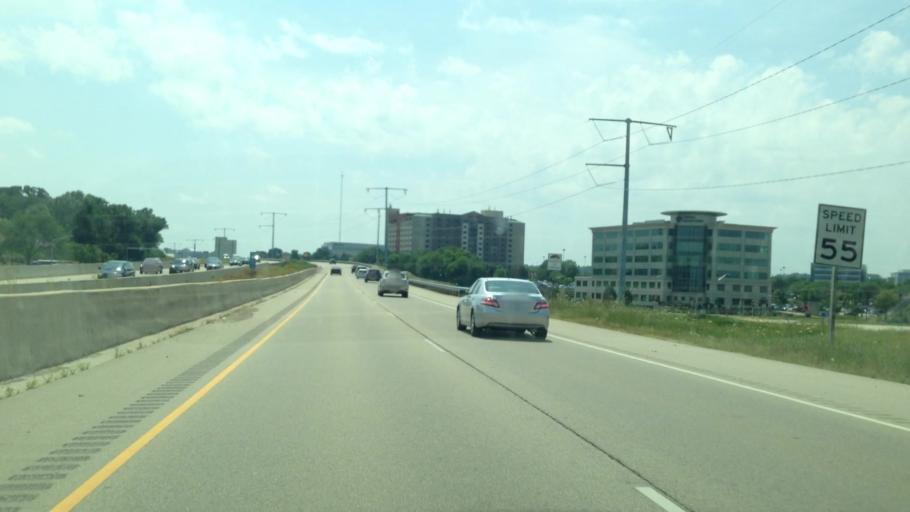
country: US
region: Wisconsin
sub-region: Dane County
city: Middleton
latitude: 43.0920
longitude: -89.5202
